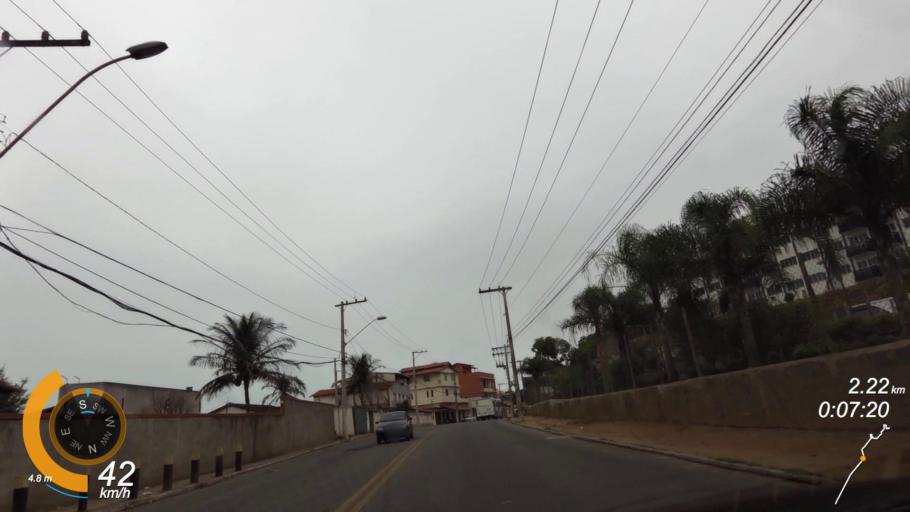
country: BR
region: Espirito Santo
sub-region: Guarapari
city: Guarapari
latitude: -20.6797
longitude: -40.5042
